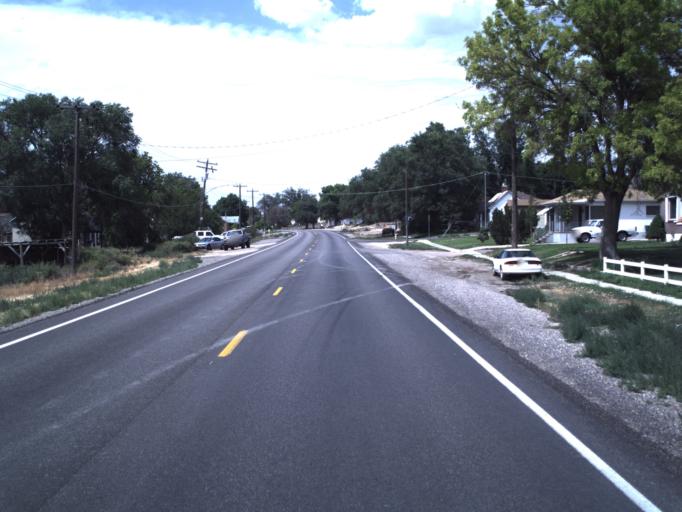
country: US
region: Utah
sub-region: Sanpete County
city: Moroni
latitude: 39.5287
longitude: -111.5906
